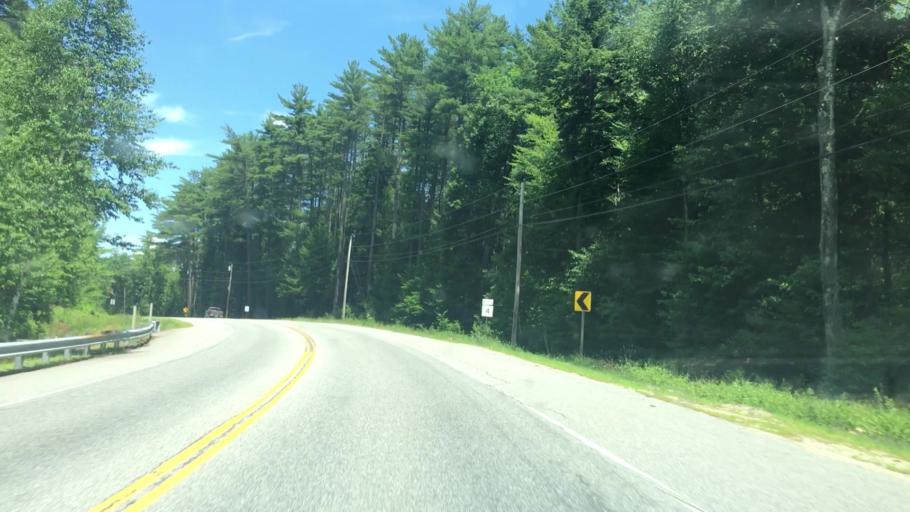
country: US
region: Maine
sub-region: Androscoggin County
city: Livermore Falls
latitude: 44.4307
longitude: -70.2124
